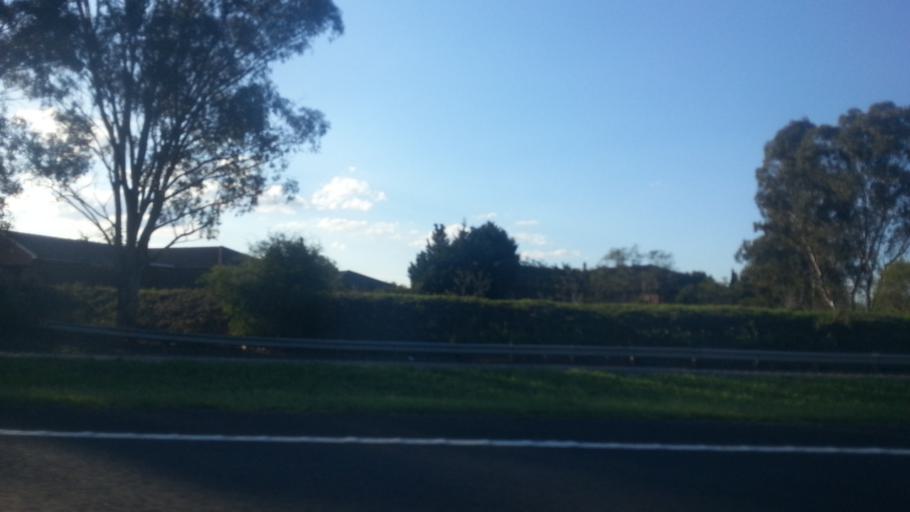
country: AU
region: New South Wales
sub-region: Camden
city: Narellan Vale
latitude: -34.0563
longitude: 150.7338
